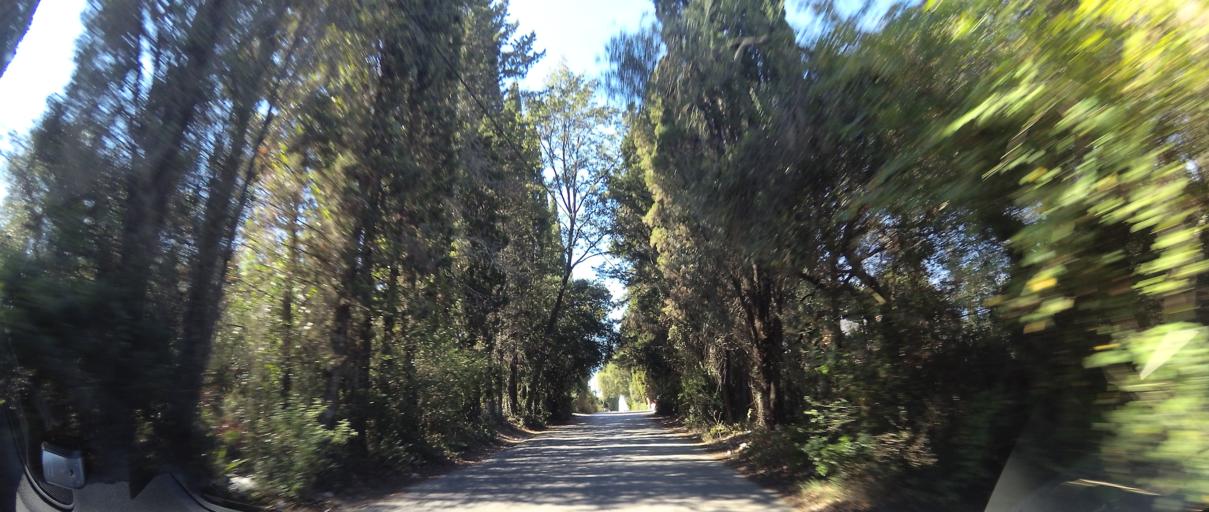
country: GR
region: Ionian Islands
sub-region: Nomos Kerkyras
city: Kontokali
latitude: 39.6419
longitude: 19.8516
